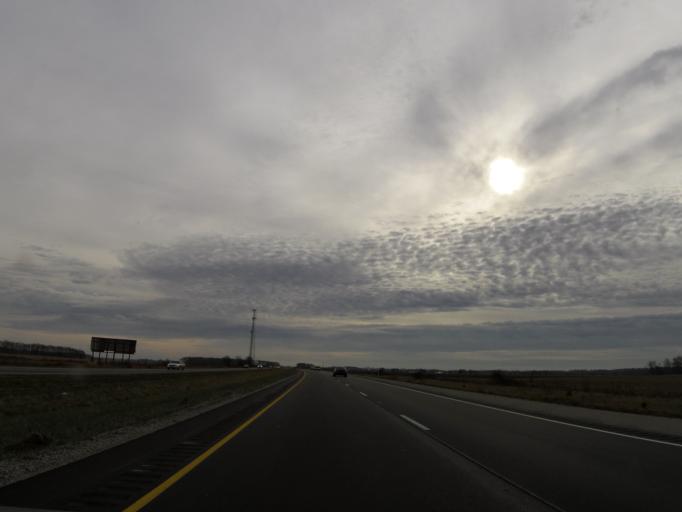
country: US
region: Indiana
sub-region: Montgomery County
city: Crawfordsville
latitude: 40.0239
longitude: -86.7830
